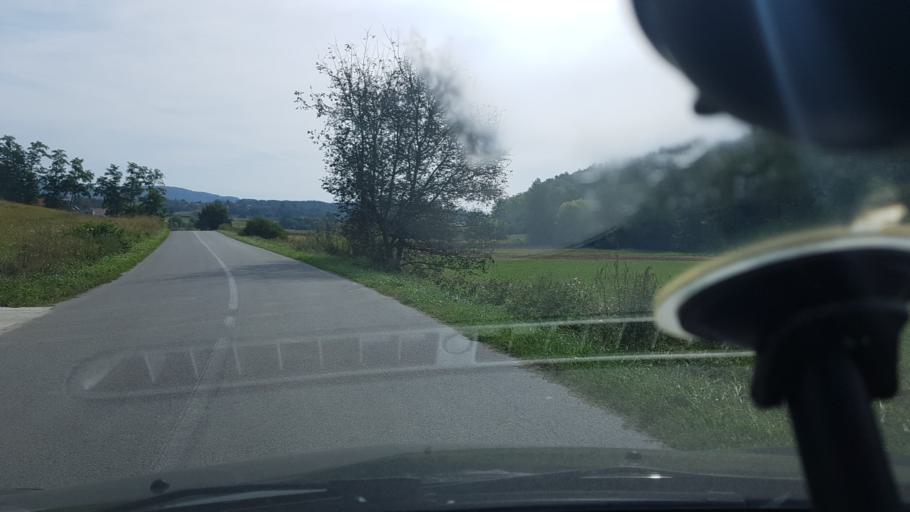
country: HR
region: Varazdinska
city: Remetinec
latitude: 46.1090
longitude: 16.2490
